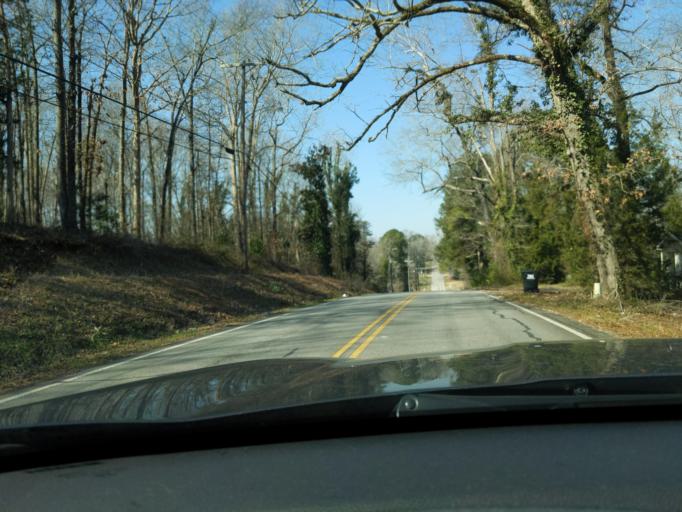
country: US
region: South Carolina
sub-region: Abbeville County
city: Calhoun Falls
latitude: 34.0891
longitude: -82.5911
